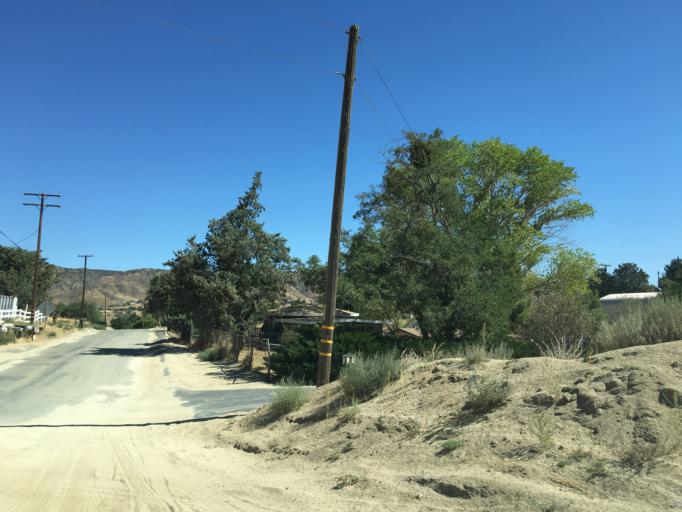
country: US
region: California
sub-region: Los Angeles County
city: Leona Valley
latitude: 34.6022
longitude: -118.2827
